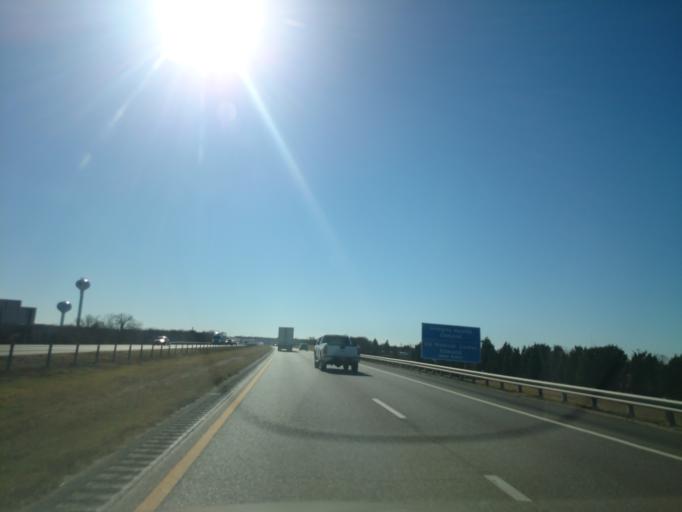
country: US
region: Oklahoma
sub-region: Oklahoma County
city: Edmond
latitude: 35.6638
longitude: -97.4225
